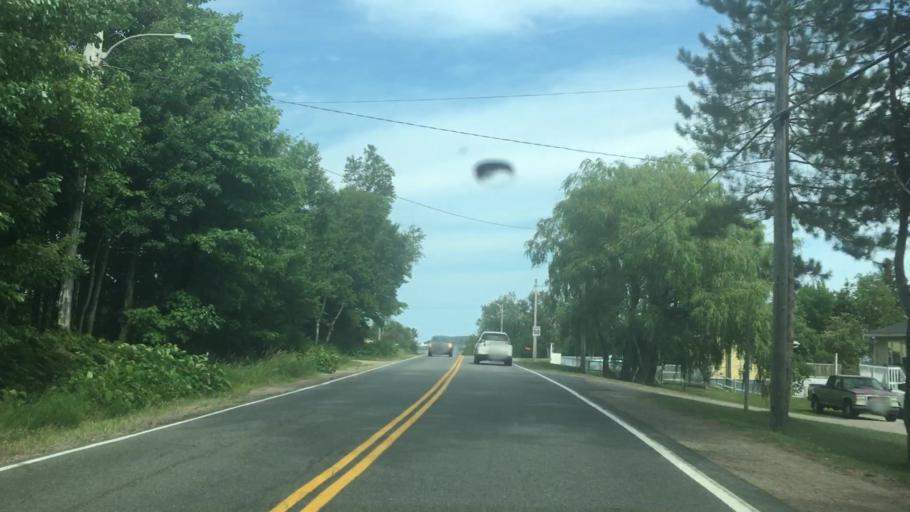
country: CA
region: Nova Scotia
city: Sydney Mines
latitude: 46.6361
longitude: -60.4131
